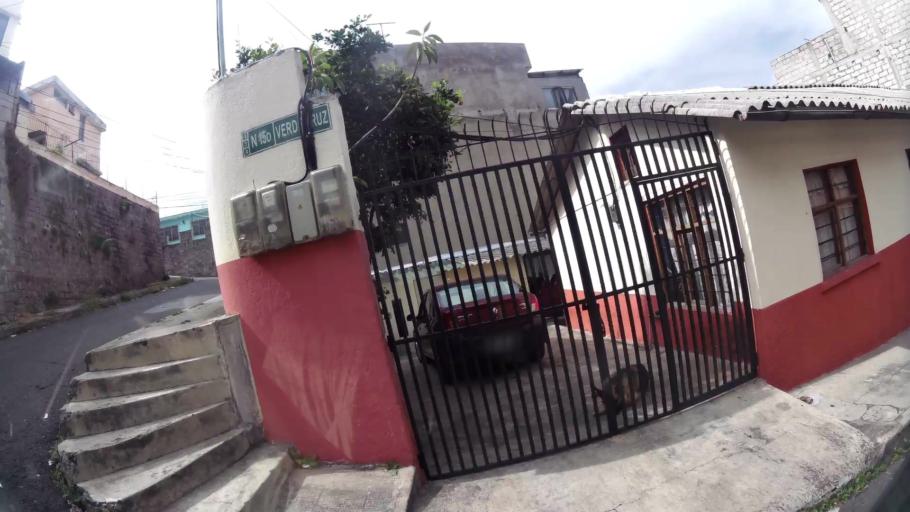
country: EC
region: Pichincha
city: Quito
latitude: -0.2186
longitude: -78.4878
